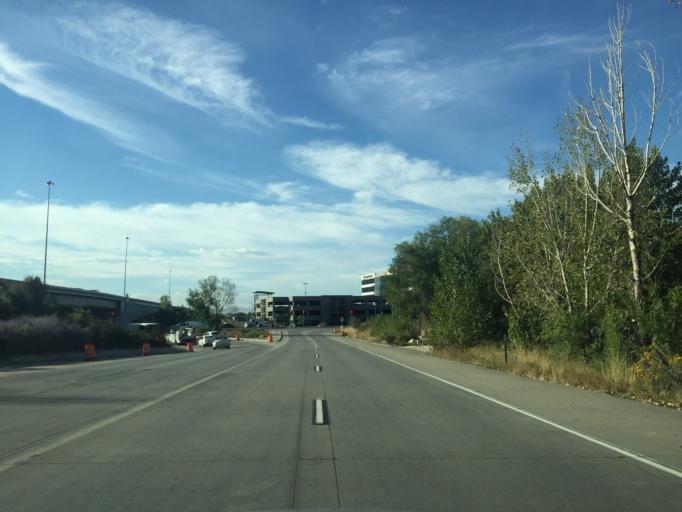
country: US
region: Utah
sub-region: Salt Lake County
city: Murray
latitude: 40.6562
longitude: -111.9023
